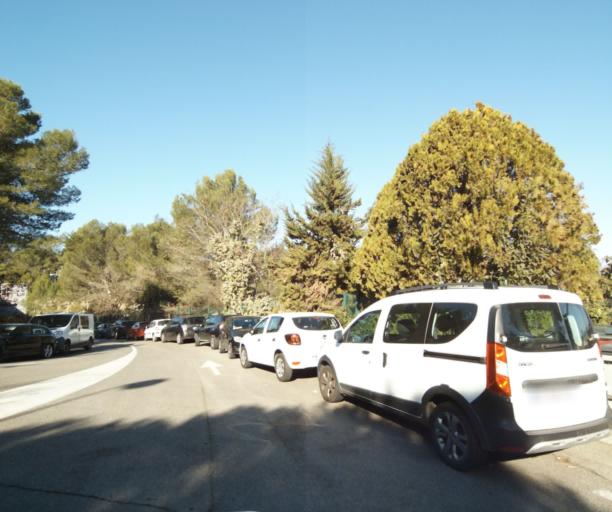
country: FR
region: Provence-Alpes-Cote d'Azur
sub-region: Departement des Alpes-Maritimes
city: Biot
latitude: 43.6069
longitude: 7.0719
